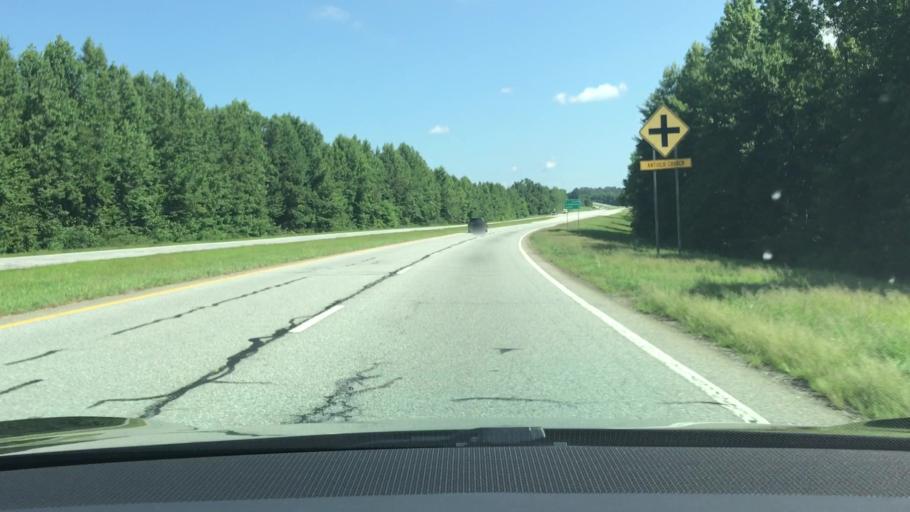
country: US
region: Georgia
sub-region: Habersham County
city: Clarkesville
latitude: 34.6102
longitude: -83.4493
